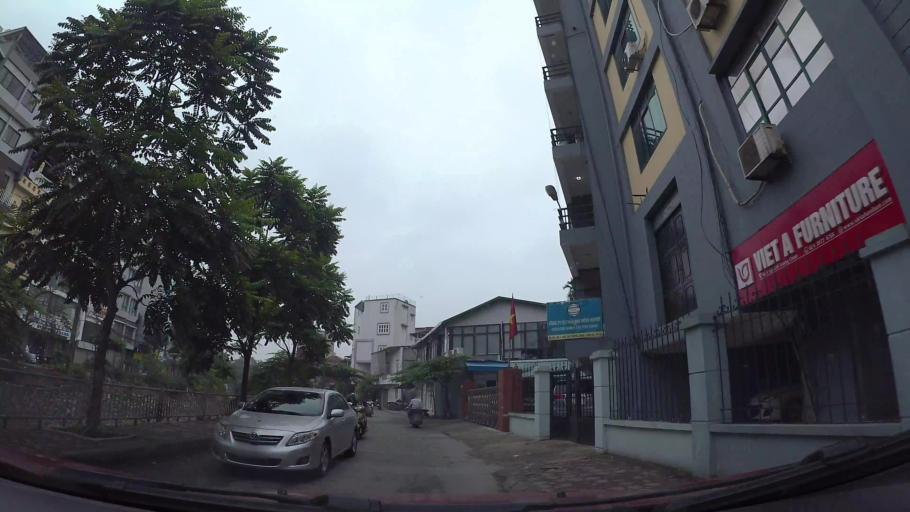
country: VN
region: Ha Noi
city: Hai BaTrung
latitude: 21.0014
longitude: 105.8347
